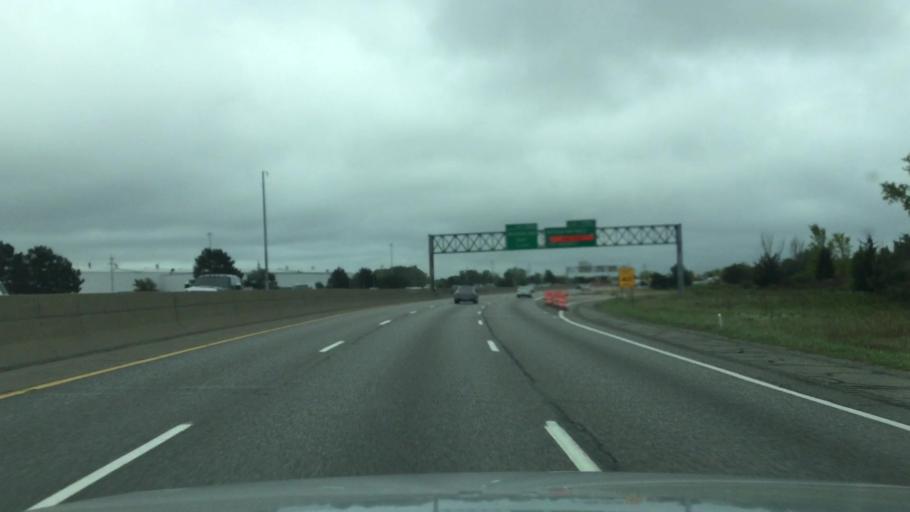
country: US
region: Michigan
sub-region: Genesee County
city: Flint
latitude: 42.9786
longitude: -83.7273
